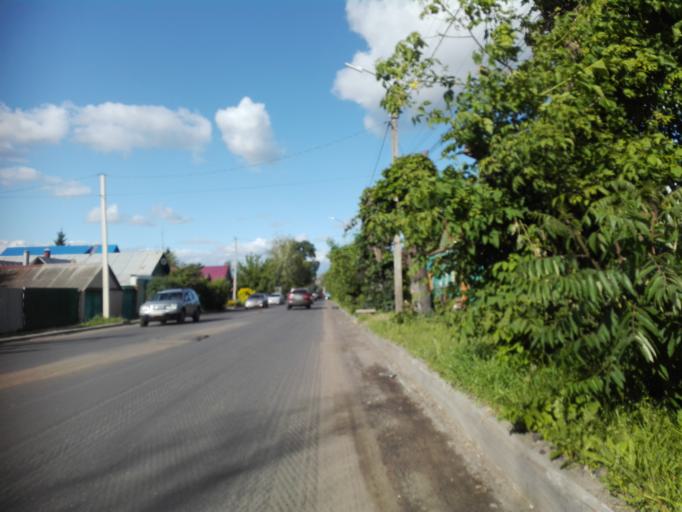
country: RU
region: Orjol
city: Orel
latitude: 52.9549
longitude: 36.0498
